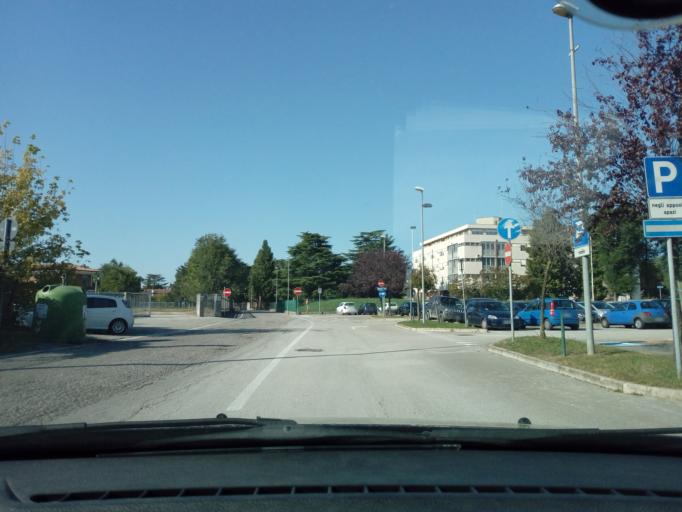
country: IT
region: Friuli Venezia Giulia
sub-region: Provincia di Gorizia
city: Cormons
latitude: 45.9582
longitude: 13.4615
